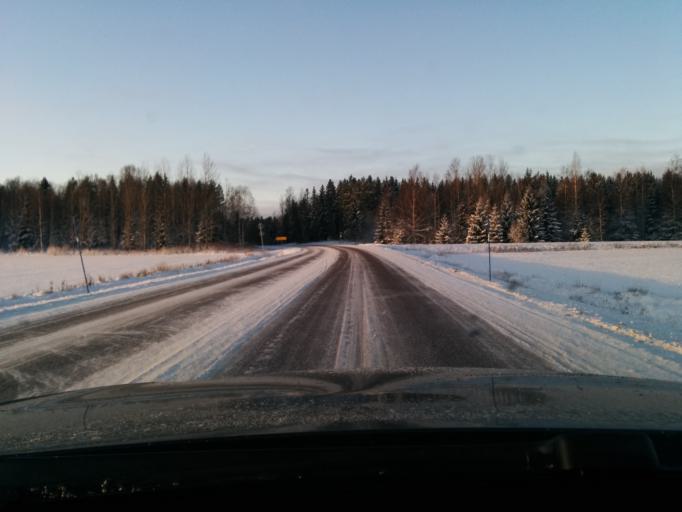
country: SE
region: Uppsala
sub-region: Tierps Kommun
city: Orbyhus
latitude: 60.1802
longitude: 17.6125
